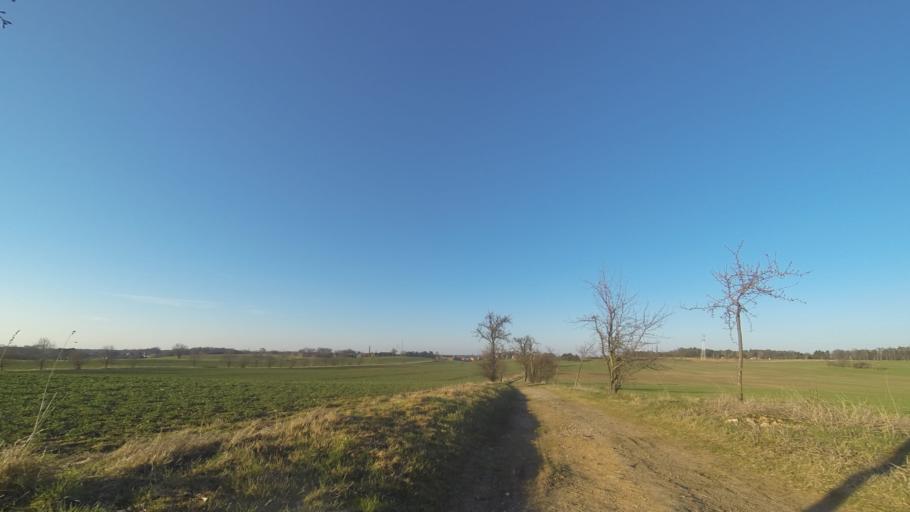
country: DE
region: Saxony
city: Ottendorf-Okrilla
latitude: 51.1577
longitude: 13.7687
